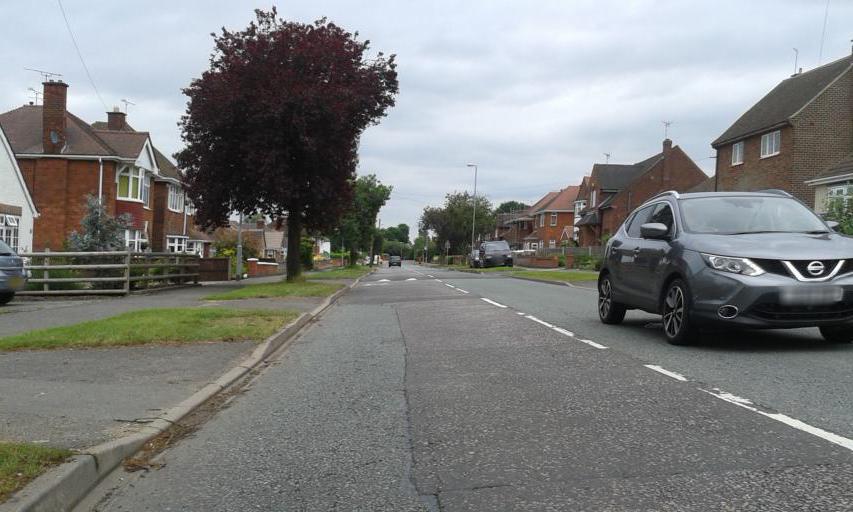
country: GB
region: England
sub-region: Leicestershire
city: Hinckley
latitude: 52.5378
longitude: -1.3579
